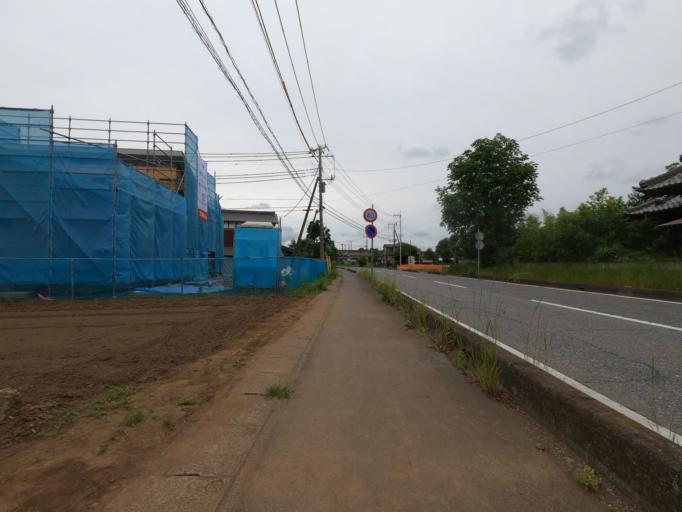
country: JP
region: Ibaraki
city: Moriya
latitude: 35.9415
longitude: 139.9702
